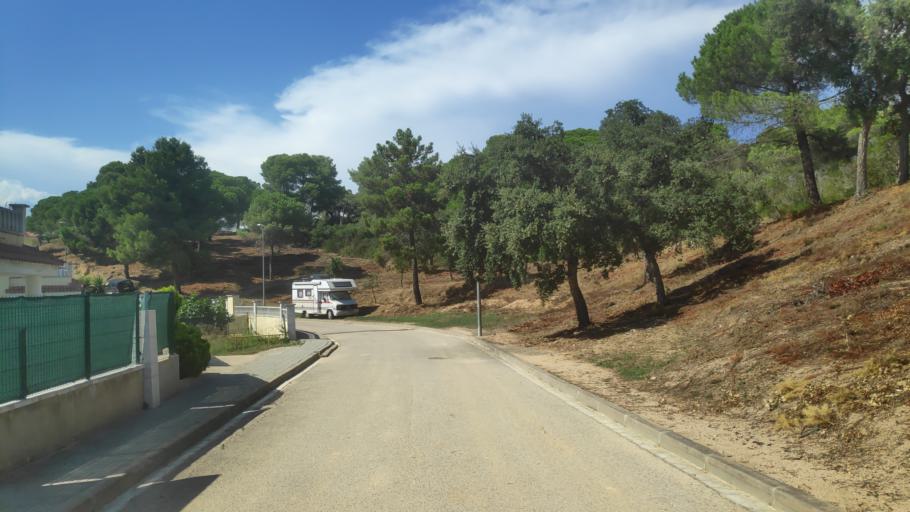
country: ES
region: Catalonia
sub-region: Provincia de Girona
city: Lloret de Mar
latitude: 41.7262
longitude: 2.8287
